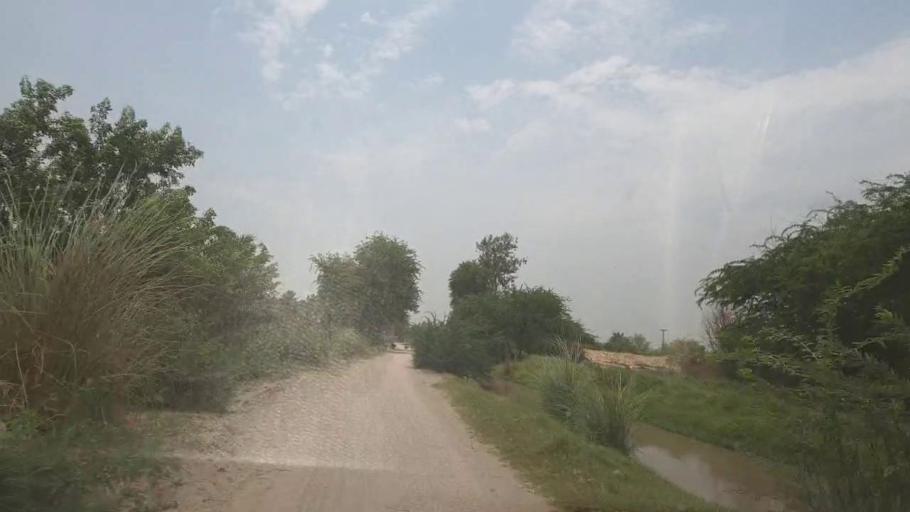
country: PK
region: Sindh
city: Kot Diji
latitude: 27.4441
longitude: 68.6766
